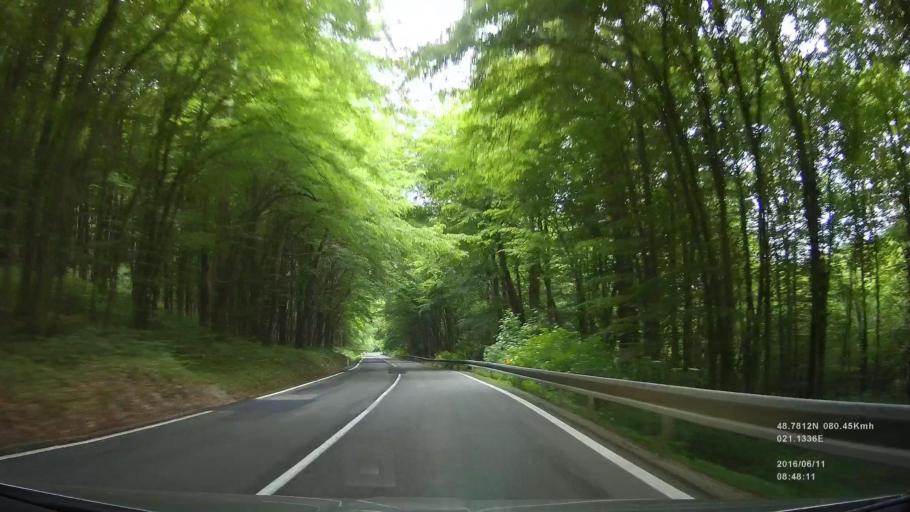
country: SK
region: Kosicky
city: Kosice
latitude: 48.7755
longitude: 21.1371
